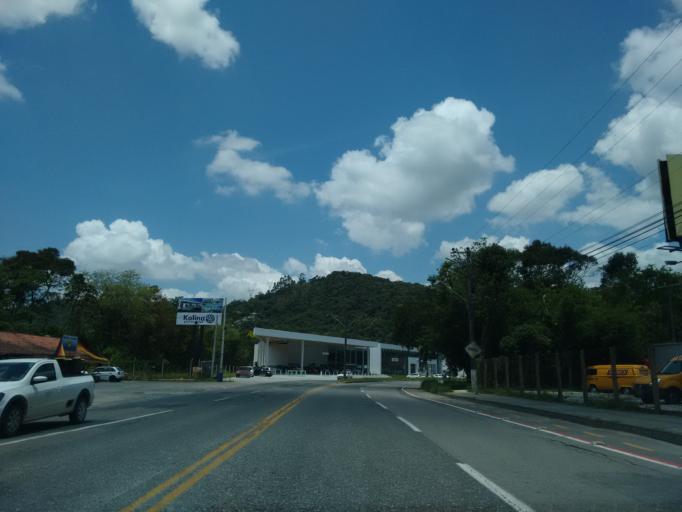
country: BR
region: Santa Catarina
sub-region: Blumenau
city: Blumenau
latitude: -26.9049
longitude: -49.0337
